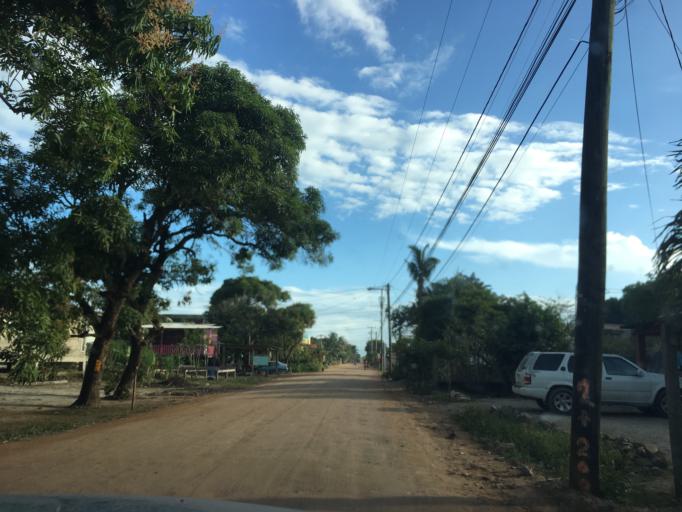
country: BZ
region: Stann Creek
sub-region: Dangriga
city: Dangriga
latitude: 16.8565
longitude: -88.2816
